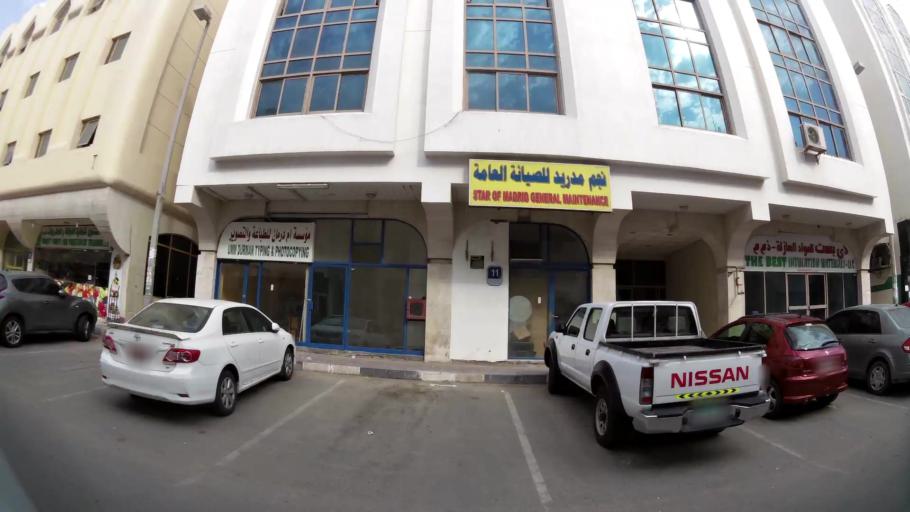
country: AE
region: Abu Dhabi
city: Abu Dhabi
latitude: 24.3232
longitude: 54.5320
